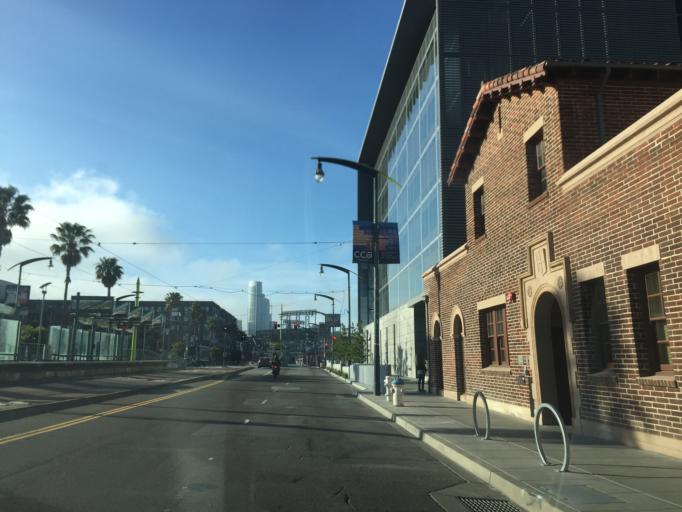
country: US
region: California
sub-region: San Francisco County
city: San Francisco
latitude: 37.7722
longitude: -122.3895
